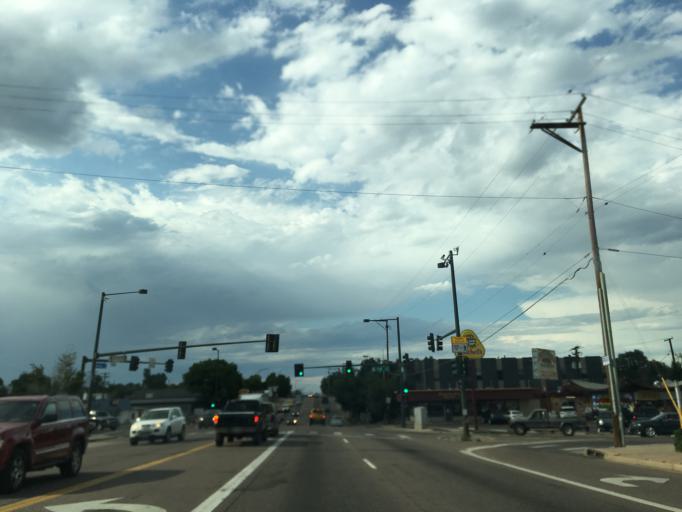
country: US
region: Colorado
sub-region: Jefferson County
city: Lakewood
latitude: 39.7178
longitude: -105.0533
